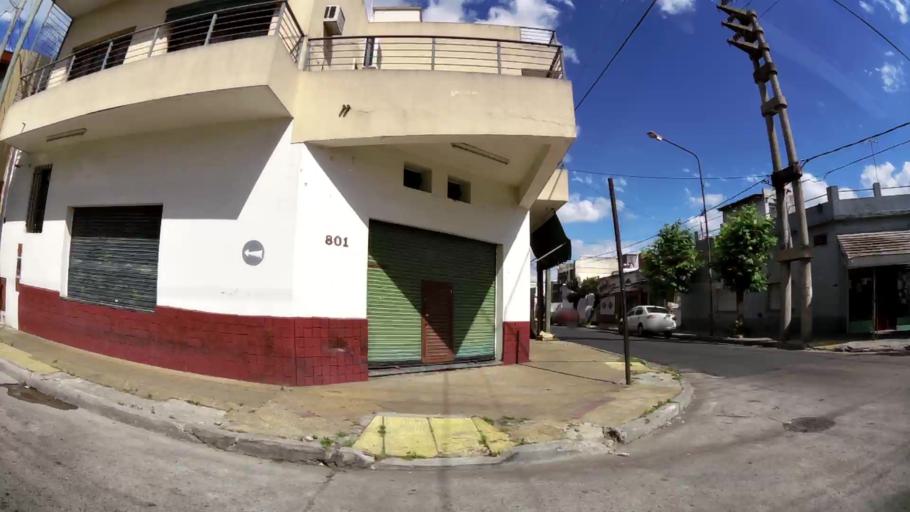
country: AR
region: Buenos Aires
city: San Justo
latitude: -34.6466
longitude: -58.5447
